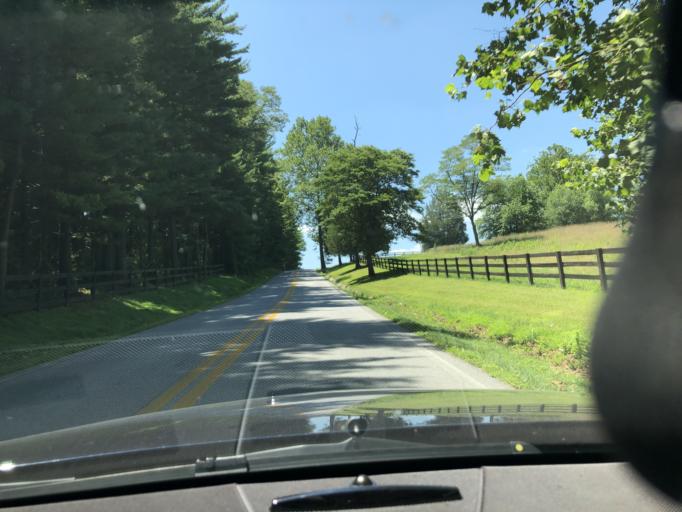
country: US
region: Maryland
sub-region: Carroll County
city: Westminster
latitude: 39.5093
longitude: -76.9327
